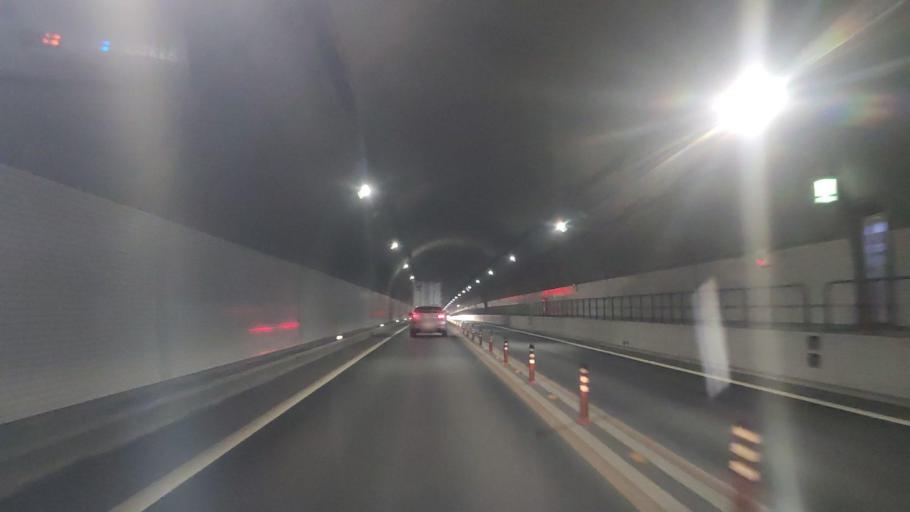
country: JP
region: Fukuoka
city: Kanda
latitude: 33.7625
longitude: 130.9620
